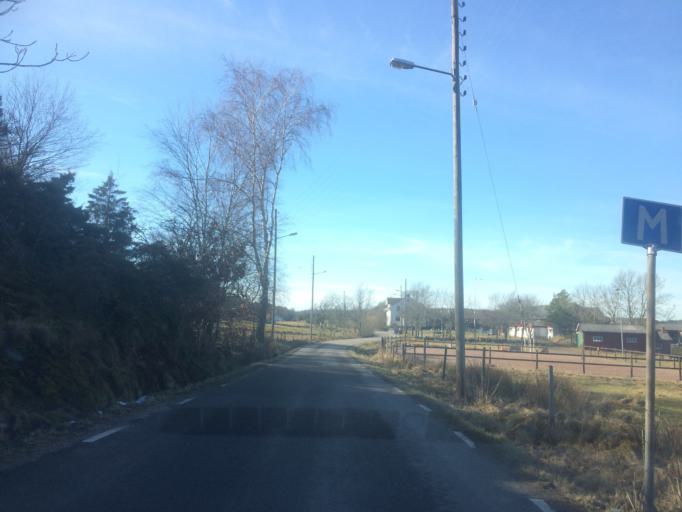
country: SE
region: Vaestra Goetaland
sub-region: Goteborg
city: Torslanda
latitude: 57.7902
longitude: 11.8573
